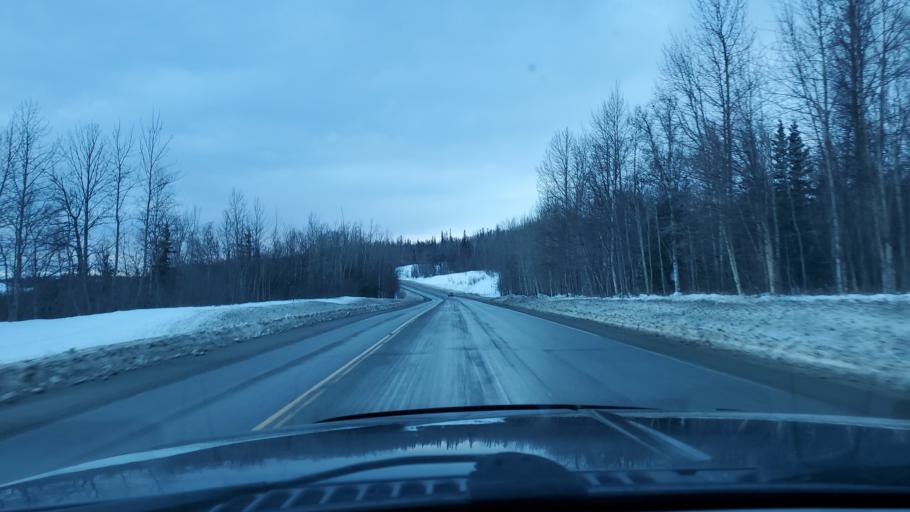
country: US
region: Alaska
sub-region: Matanuska-Susitna Borough
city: Lazy Mountain
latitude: 61.7112
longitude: -148.9136
